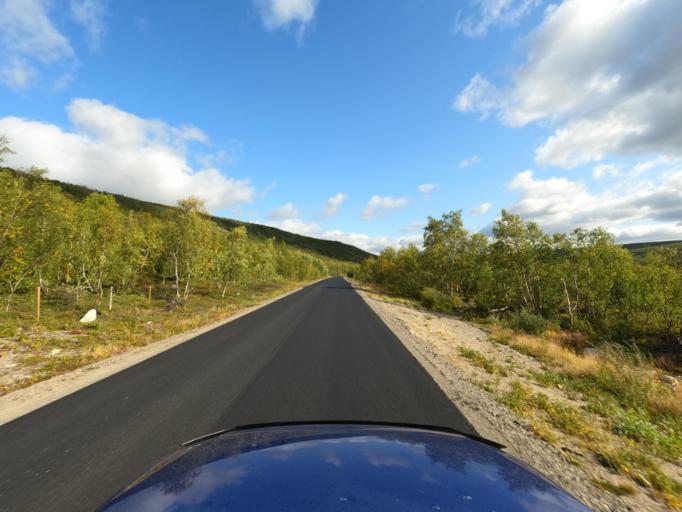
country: NO
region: Finnmark Fylke
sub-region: Porsanger
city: Lakselv
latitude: 69.4048
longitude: 24.6651
